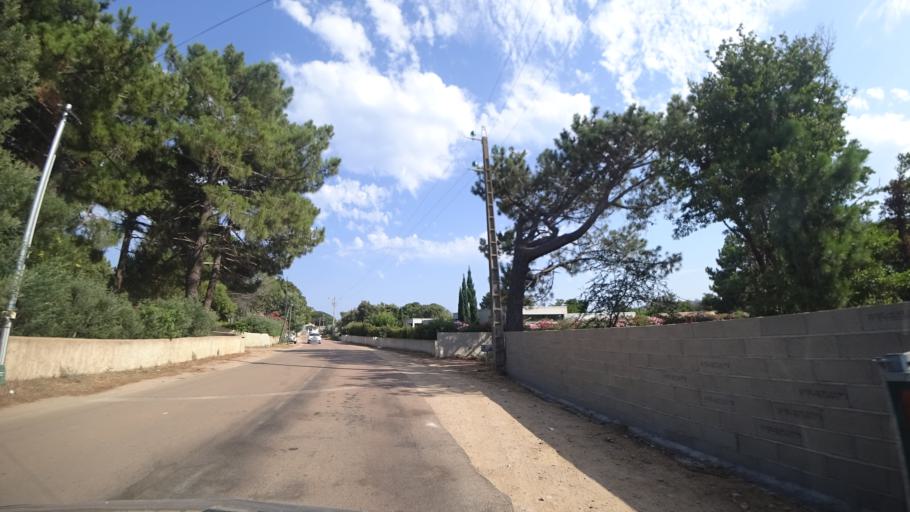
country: FR
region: Corsica
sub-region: Departement de la Corse-du-Sud
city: Porto-Vecchio
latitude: 41.6308
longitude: 9.3324
